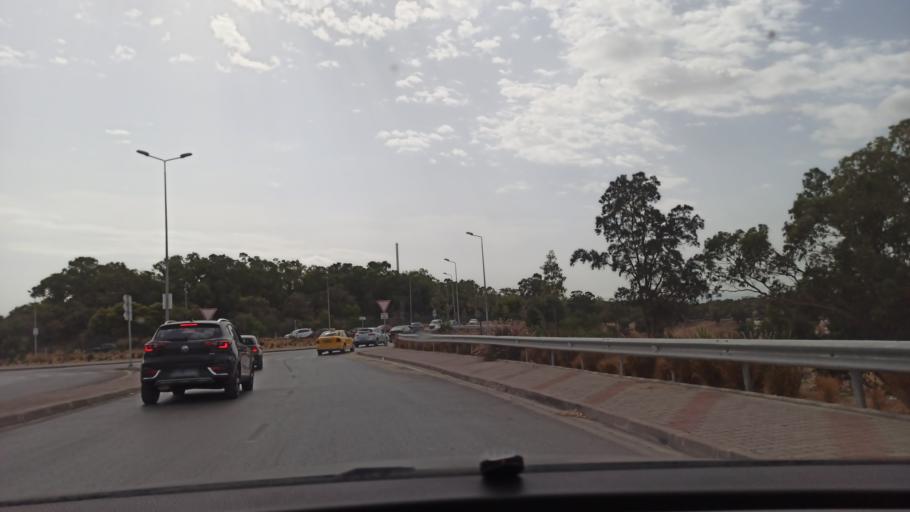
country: TN
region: Tunis
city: Tunis
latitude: 36.8288
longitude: 10.1660
